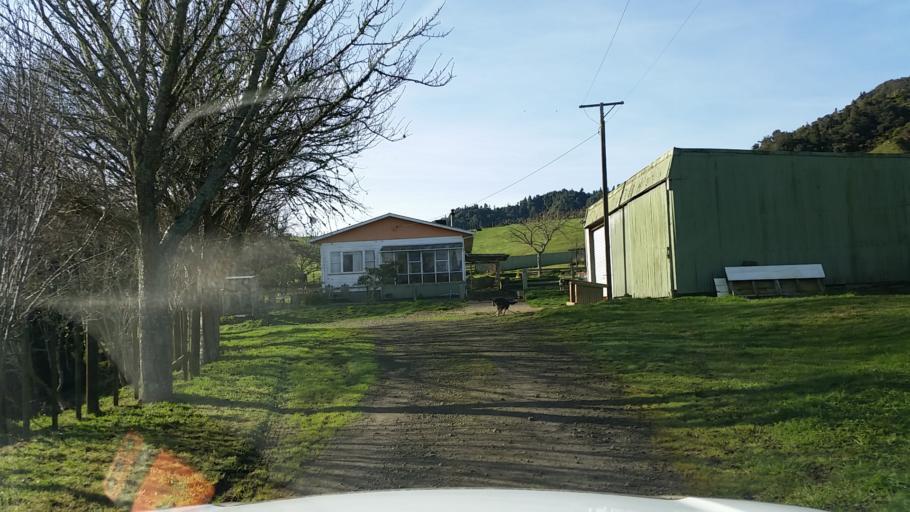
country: NZ
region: Taranaki
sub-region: South Taranaki District
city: Eltham
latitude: -39.3105
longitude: 174.5505
